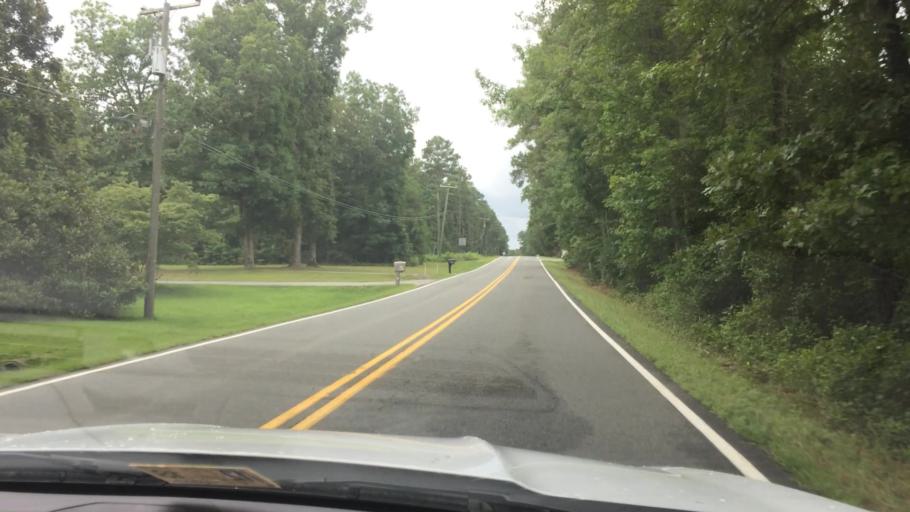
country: US
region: Virginia
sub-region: New Kent County
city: New Kent
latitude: 37.4711
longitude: -77.0329
